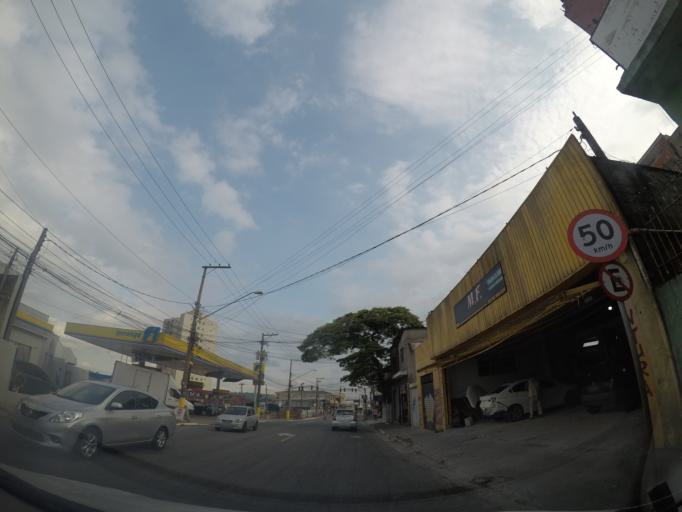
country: BR
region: Sao Paulo
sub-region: Guarulhos
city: Guarulhos
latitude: -23.4266
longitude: -46.5034
